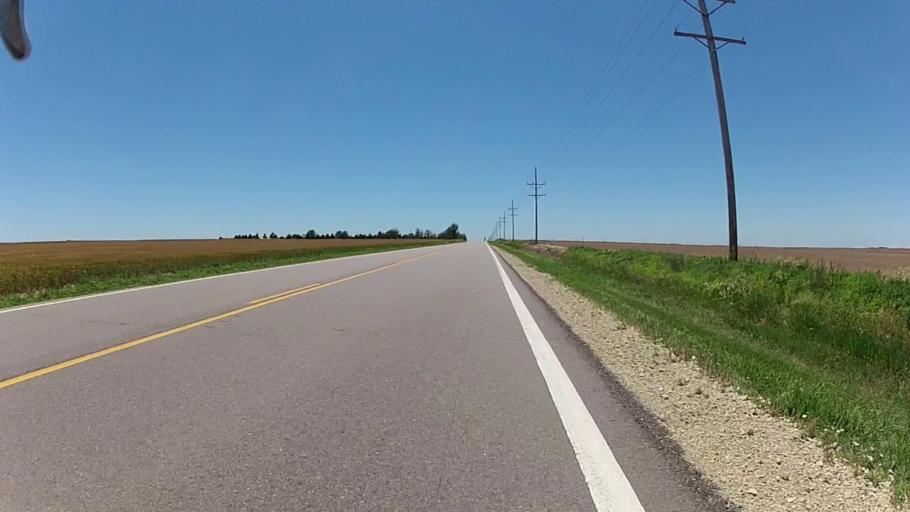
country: US
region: Kansas
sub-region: Kiowa County
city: Greensburg
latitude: 37.5225
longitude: -99.3206
